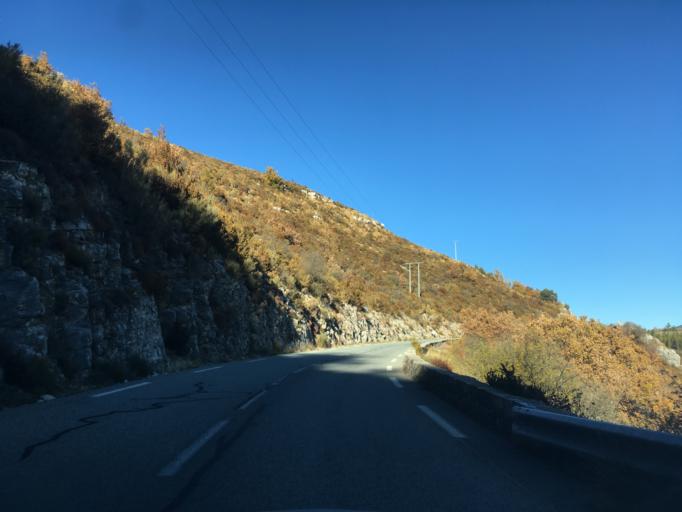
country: FR
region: Provence-Alpes-Cote d'Azur
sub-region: Departement du Var
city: Montferrat
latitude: 43.6791
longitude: 6.5072
